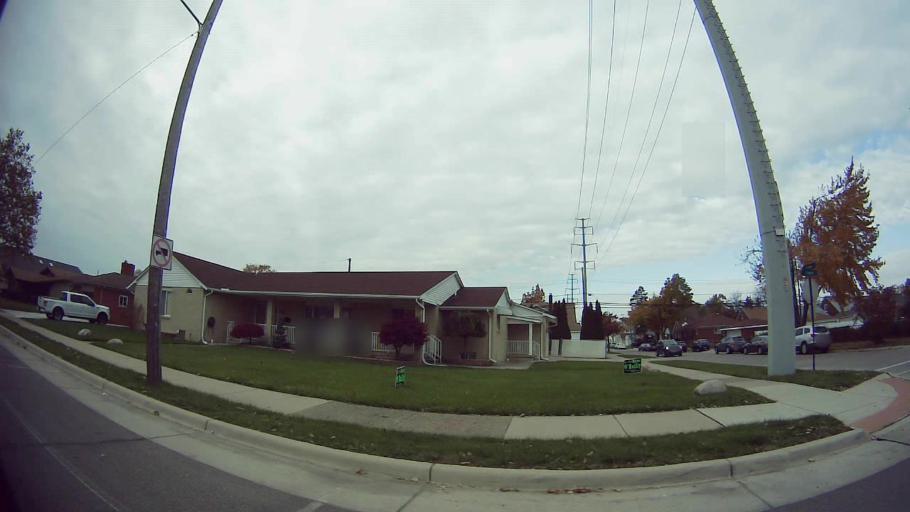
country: US
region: Michigan
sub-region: Wayne County
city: Dearborn
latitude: 42.3381
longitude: -83.1863
